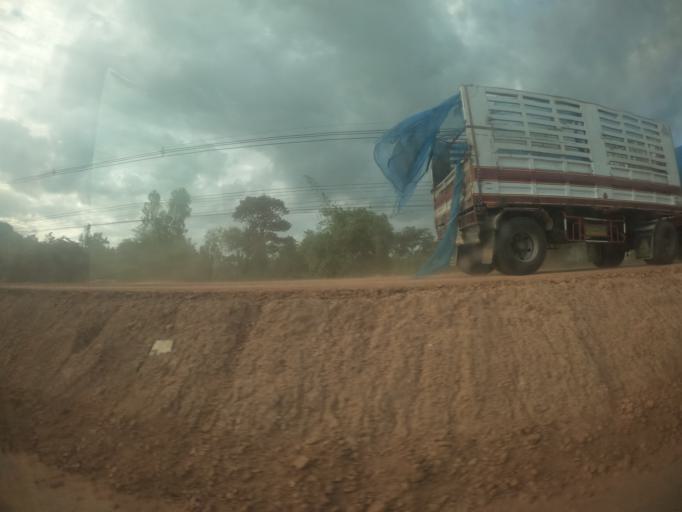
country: TH
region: Surin
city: Kap Choeng
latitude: 14.4639
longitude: 103.6452
